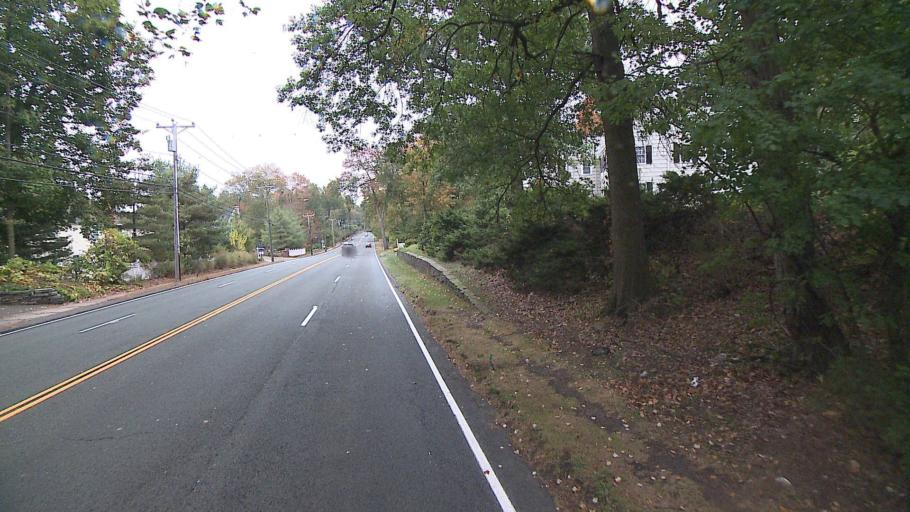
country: US
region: Connecticut
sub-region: Hartford County
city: West Hartford
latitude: 41.7863
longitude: -72.7216
